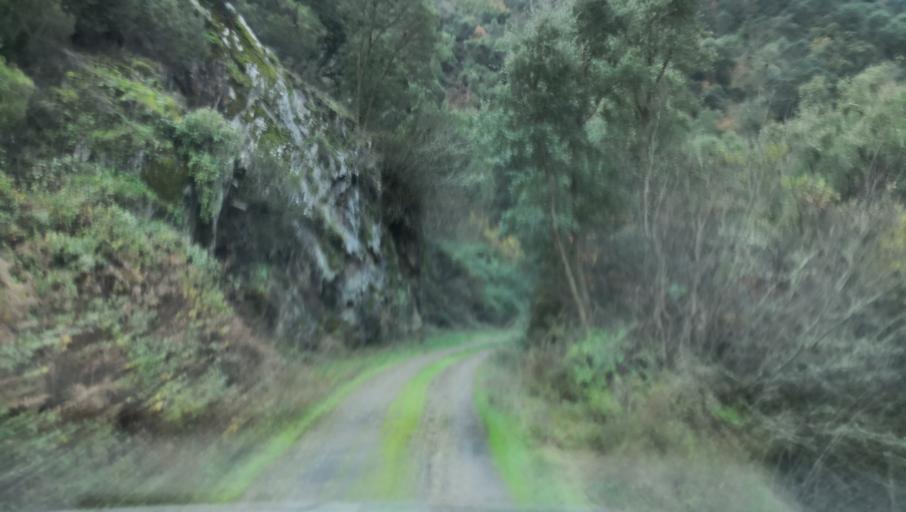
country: PT
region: Vila Real
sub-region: Santa Marta de Penaguiao
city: Santa Marta de Penaguiao
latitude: 41.2140
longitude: -7.7568
